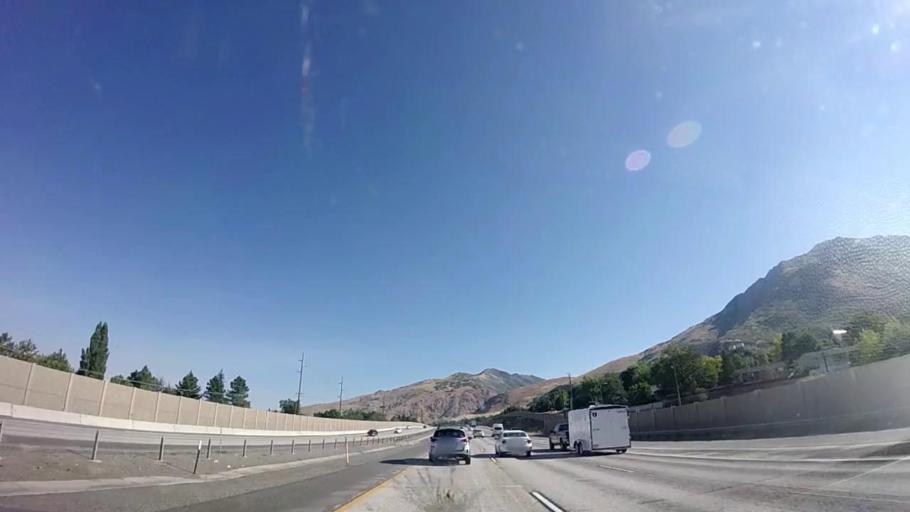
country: US
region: Utah
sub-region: Salt Lake County
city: Mount Olympus
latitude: 40.6926
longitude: -111.7967
